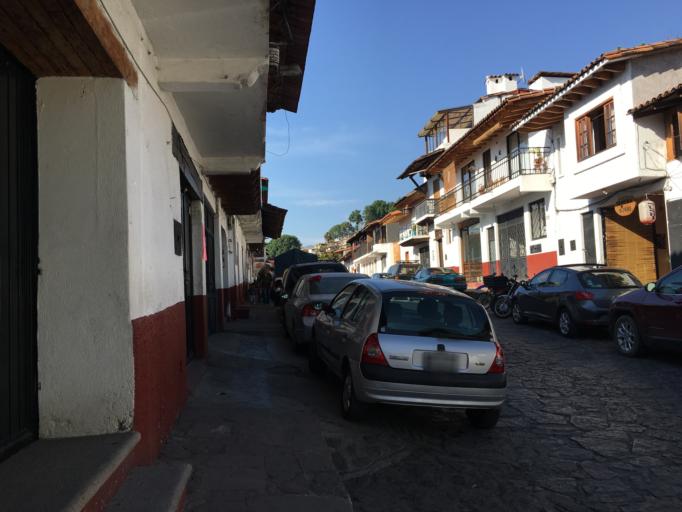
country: MX
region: Mexico
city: Valle de Bravo
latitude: 19.1879
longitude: -100.1284
